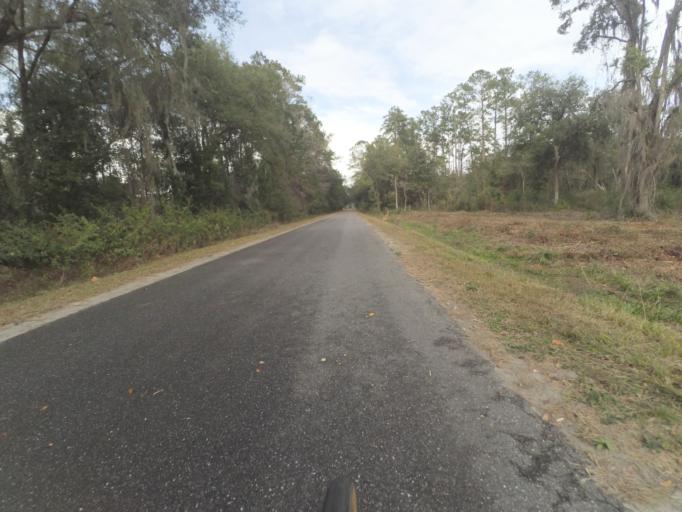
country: US
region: Florida
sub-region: Alachua County
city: Gainesville
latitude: 29.6281
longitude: -82.3114
